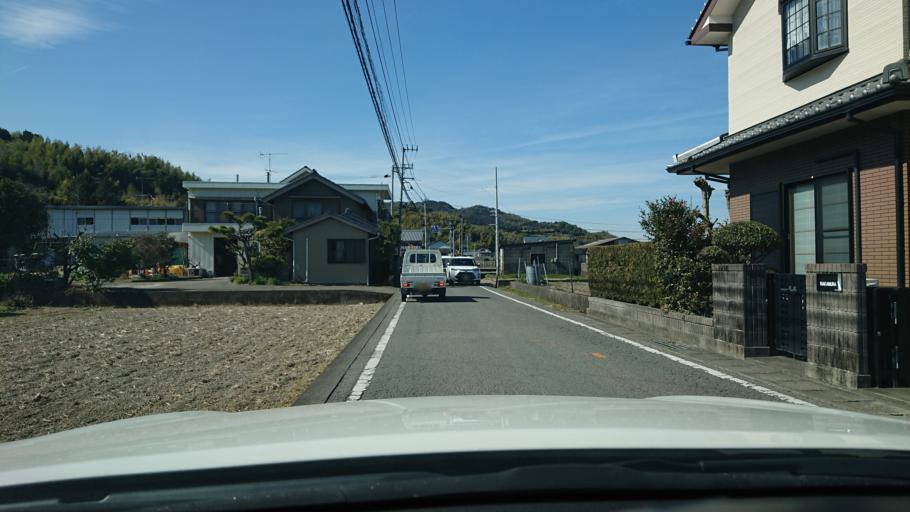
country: JP
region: Tokushima
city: Komatsushimacho
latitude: 33.9797
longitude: 134.5891
